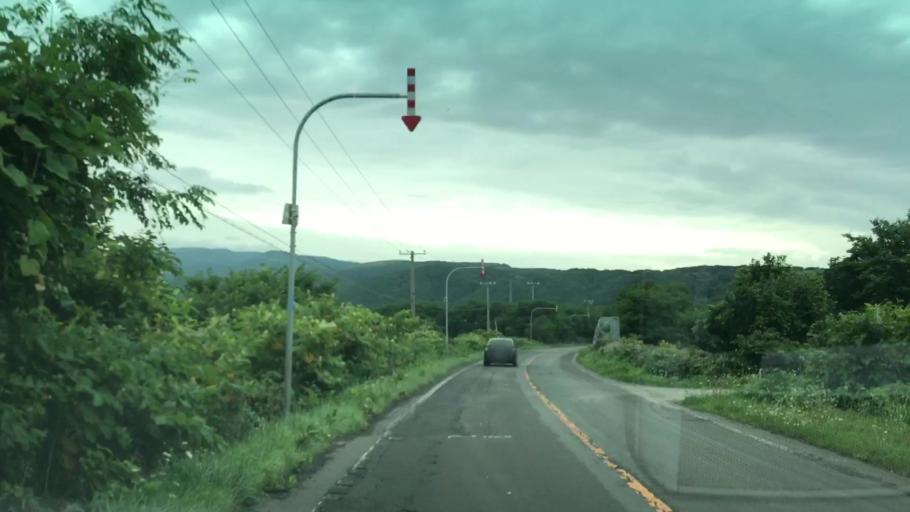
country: JP
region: Hokkaido
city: Iwanai
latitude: 42.8831
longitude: 140.3729
